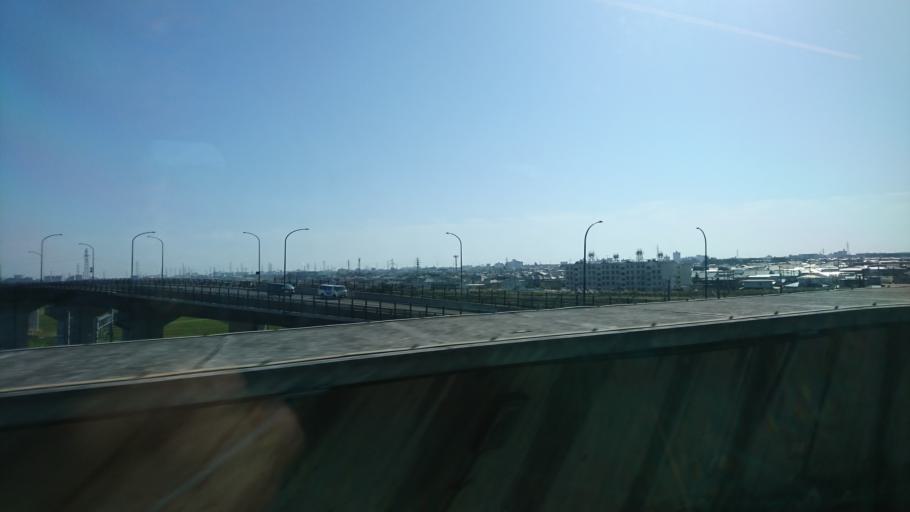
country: JP
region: Miyagi
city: Rifu
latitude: 38.3034
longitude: 140.9586
